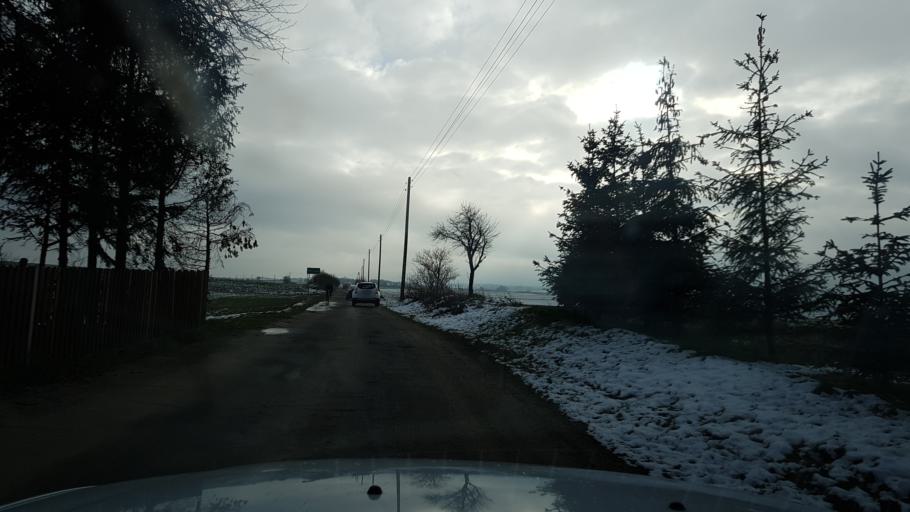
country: PL
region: West Pomeranian Voivodeship
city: Trzcinsko Zdroj
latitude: 52.9614
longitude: 14.6759
